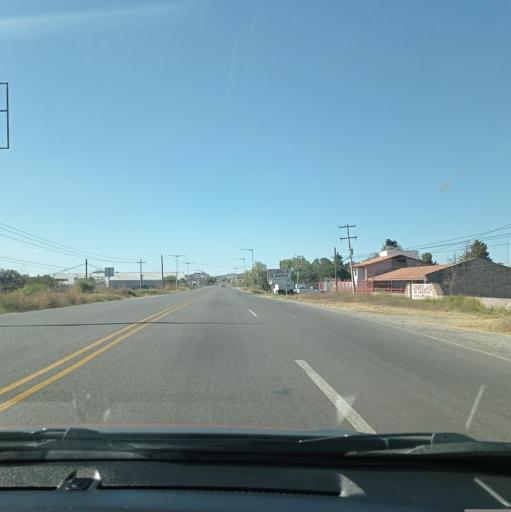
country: MX
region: Jalisco
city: San Miguel el Alto
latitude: 21.0282
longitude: -102.3836
